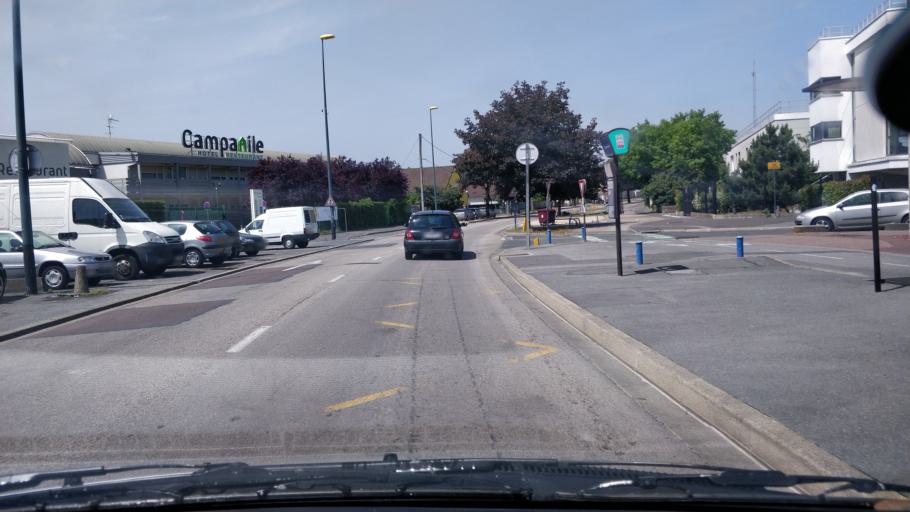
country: FR
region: Ile-de-France
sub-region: Departement de Seine-et-Marne
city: Chelles
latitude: 48.8779
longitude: 2.6020
